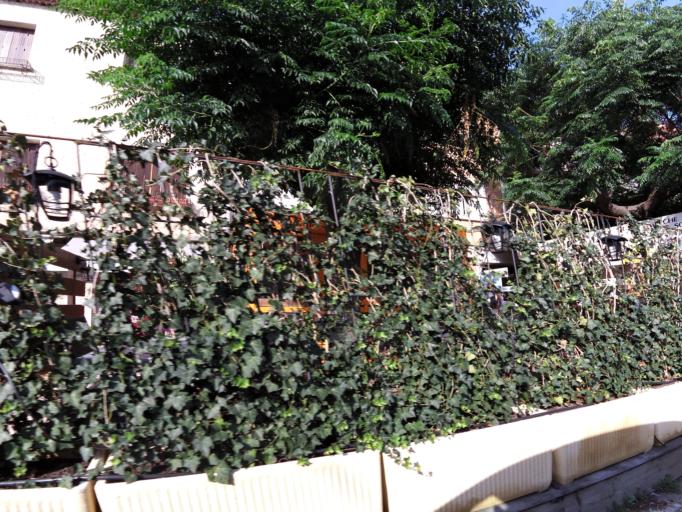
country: FR
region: Provence-Alpes-Cote d'Azur
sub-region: Departement du Var
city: Carqueiranne
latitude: 43.0895
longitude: 6.0769
